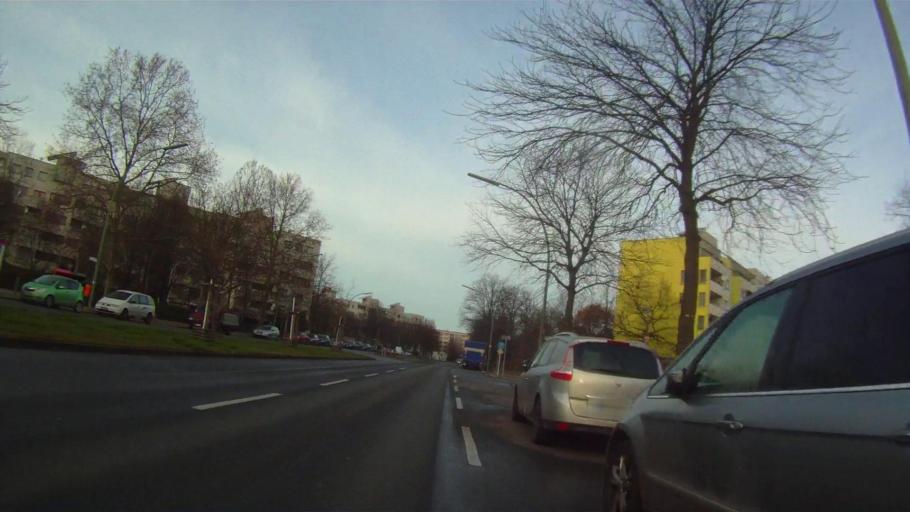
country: DE
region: Berlin
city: Baumschulenweg
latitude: 52.4623
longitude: 13.4773
